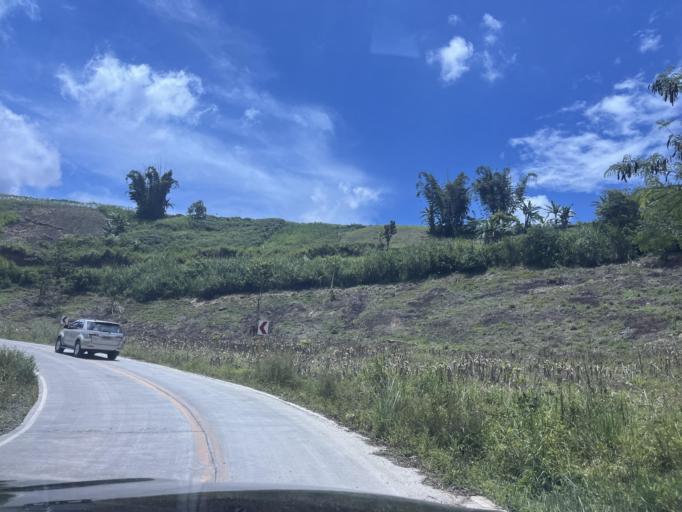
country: PH
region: Northern Mindanao
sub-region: Province of Bukidnon
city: Kisolon
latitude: 8.3098
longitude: 124.9638
